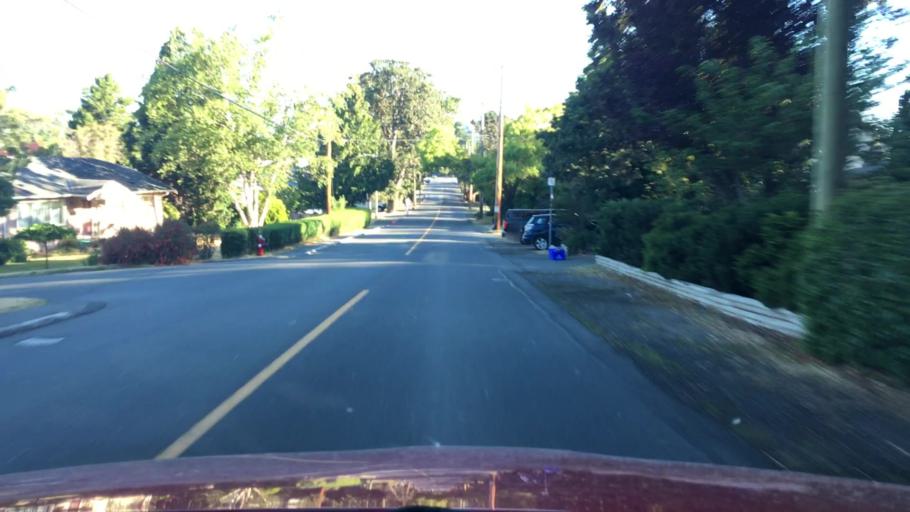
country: CA
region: British Columbia
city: Oak Bay
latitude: 48.4568
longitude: -123.3285
